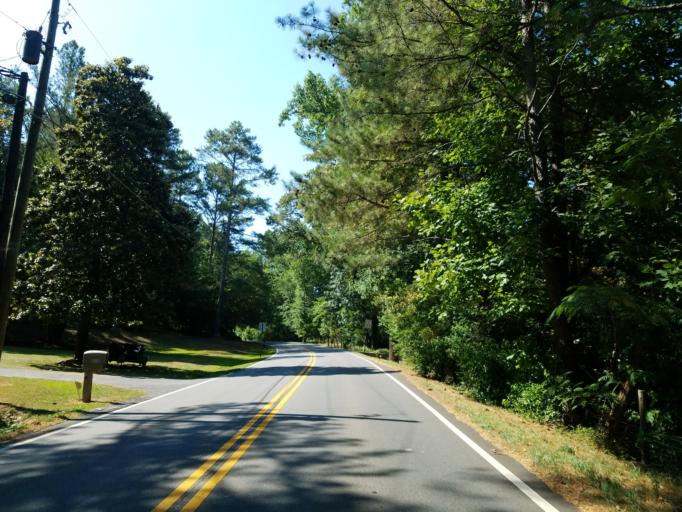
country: US
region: Georgia
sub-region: Fulton County
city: Milton
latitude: 34.1164
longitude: -84.3398
